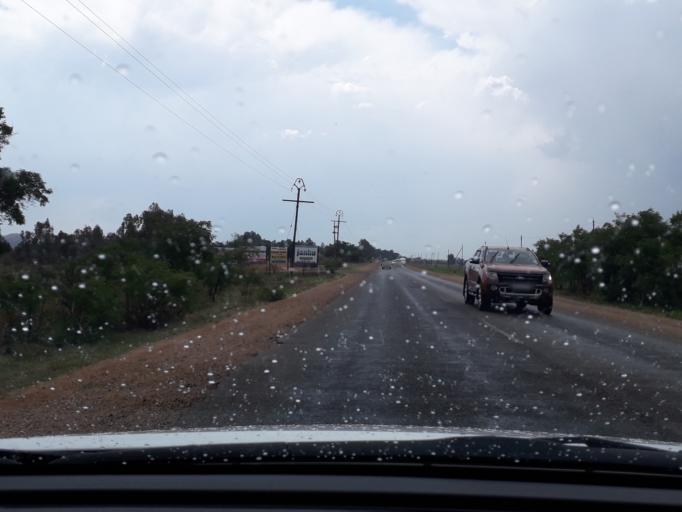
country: ZA
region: Gauteng
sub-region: West Rand District Municipality
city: Muldersdriseloop
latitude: -26.0053
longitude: 27.8580
